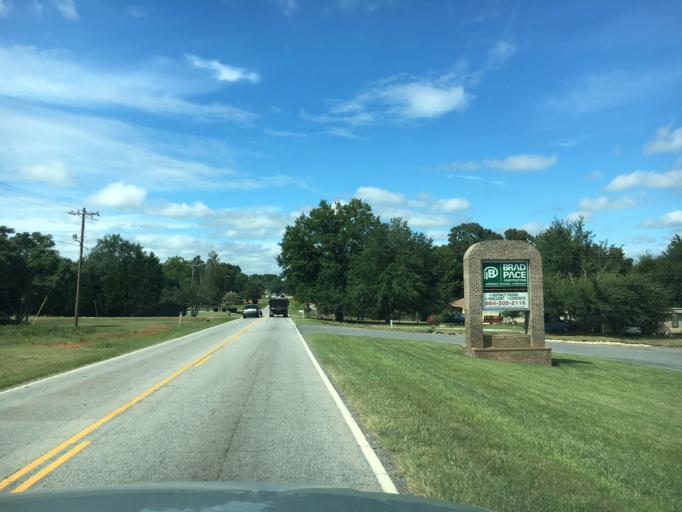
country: US
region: South Carolina
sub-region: Spartanburg County
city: Wellford
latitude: 34.9911
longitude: -82.1108
